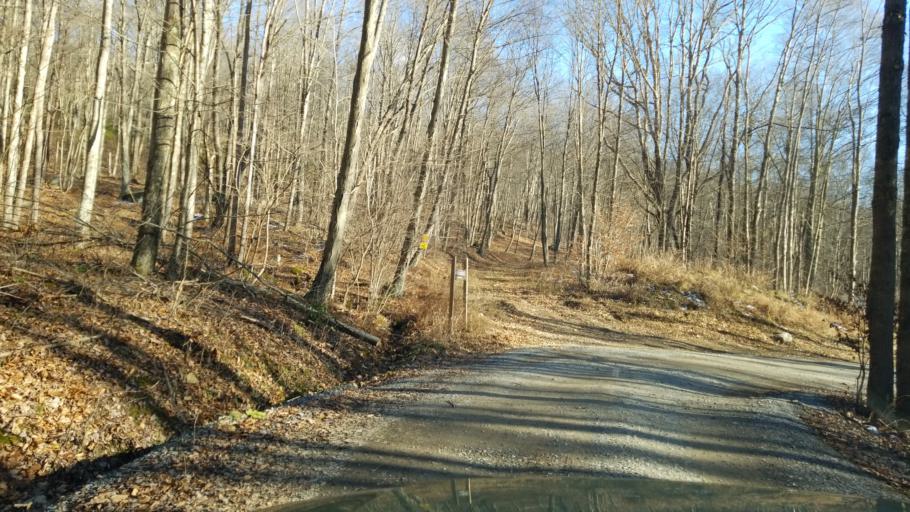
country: US
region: Pennsylvania
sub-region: Jefferson County
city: Brockway
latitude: 41.2874
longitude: -78.8289
